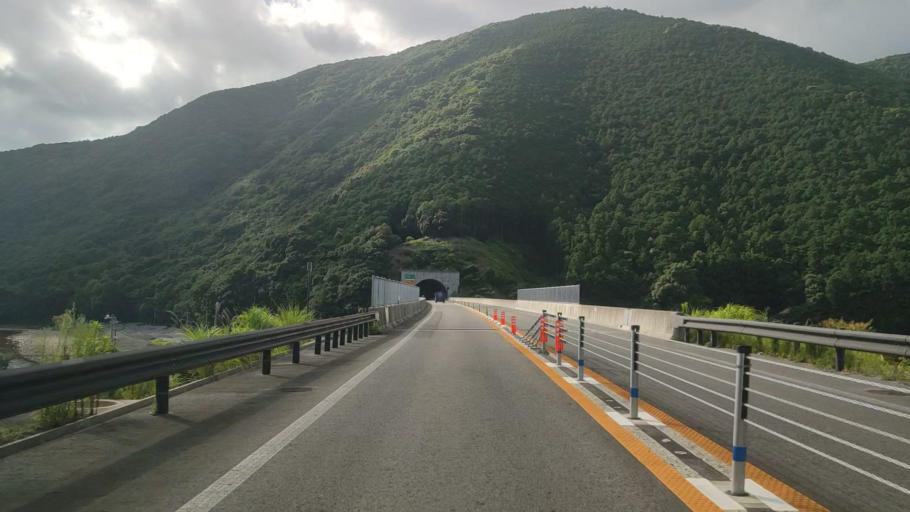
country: JP
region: Wakayama
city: Tanabe
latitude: 33.5603
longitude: 135.5054
